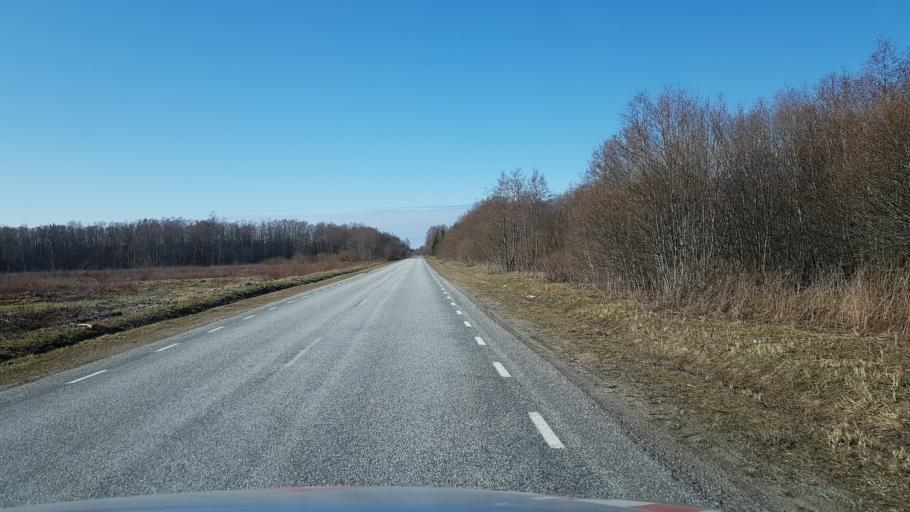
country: EE
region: Laeaene-Virumaa
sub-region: Haljala vald
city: Haljala
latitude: 59.4879
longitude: 26.1487
